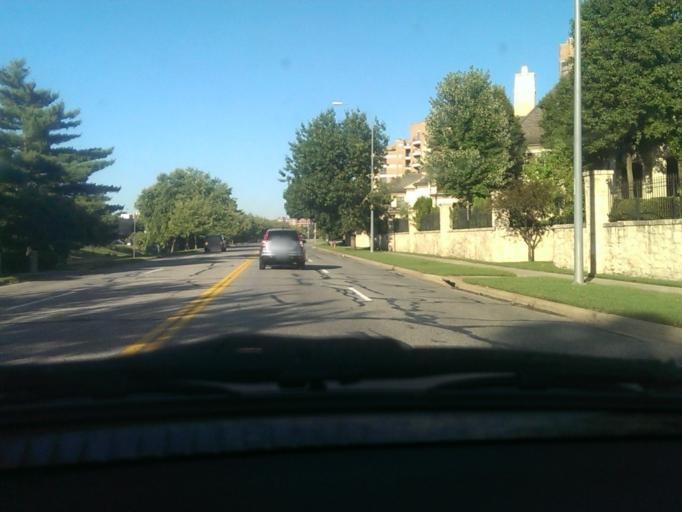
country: US
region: Kansas
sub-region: Johnson County
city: Westwood
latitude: 39.0387
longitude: -94.5966
